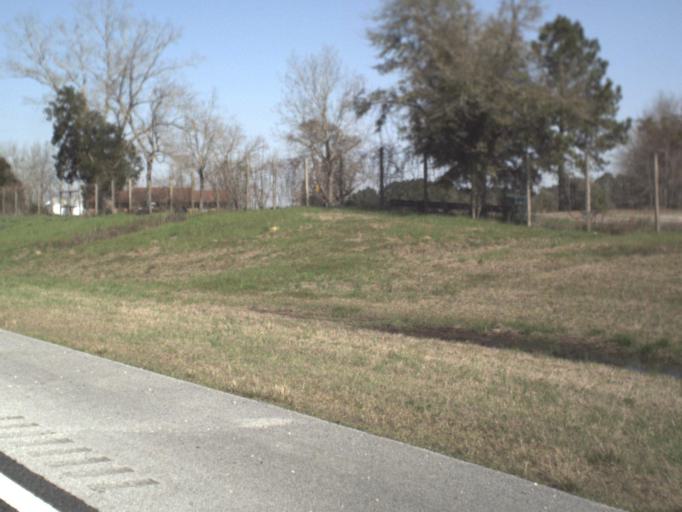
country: US
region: Florida
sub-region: Jackson County
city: Sneads
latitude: 30.6487
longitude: -85.0128
